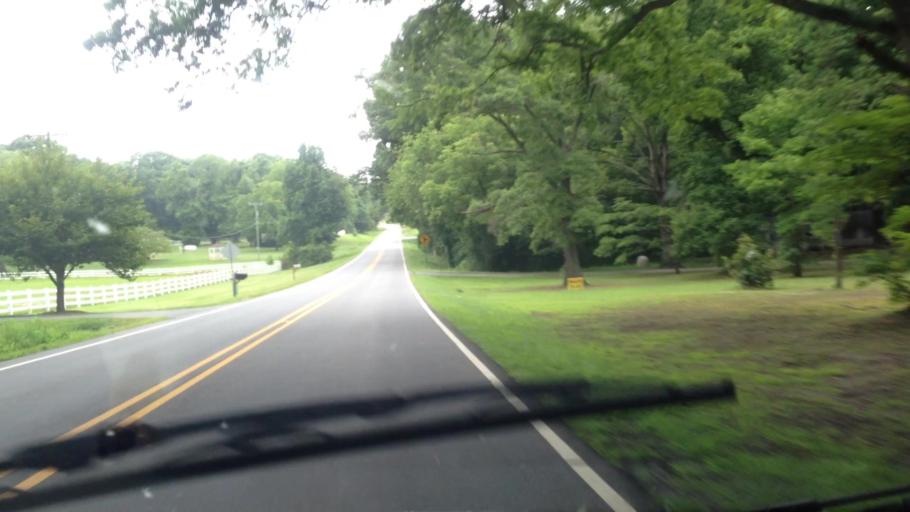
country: US
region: North Carolina
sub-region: Rockingham County
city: Mayodan
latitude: 36.4105
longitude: -80.0042
